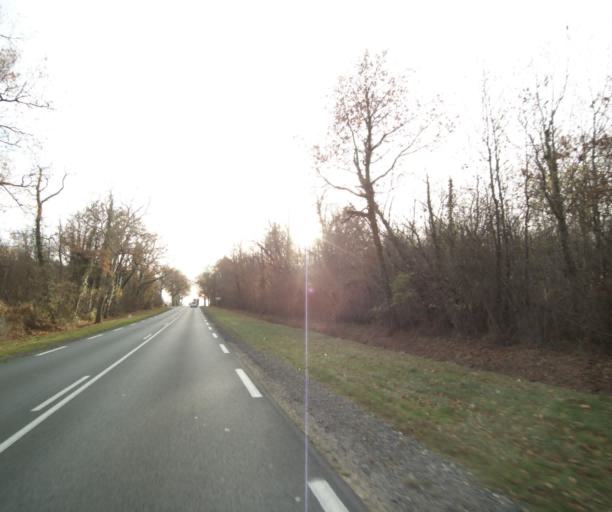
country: FR
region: Poitou-Charentes
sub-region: Departement de la Charente-Maritime
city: Saint-Hilaire-de-Villefranche
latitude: 45.8204
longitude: -0.5448
